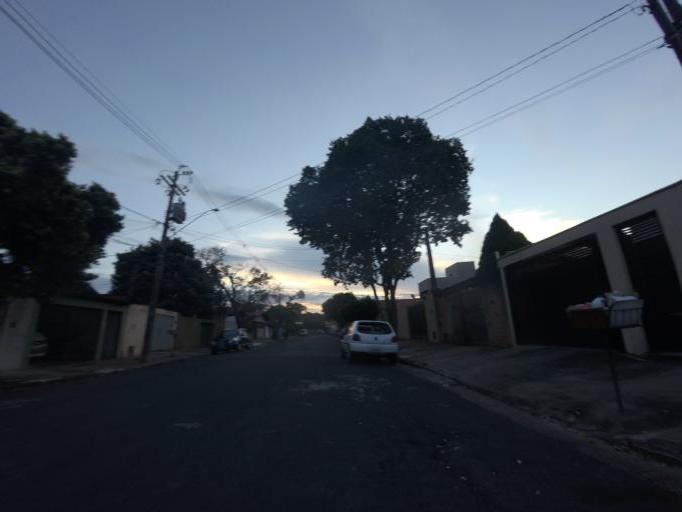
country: BR
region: Sao Paulo
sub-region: Piracicaba
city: Piracicaba
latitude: -22.7657
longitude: -47.5887
